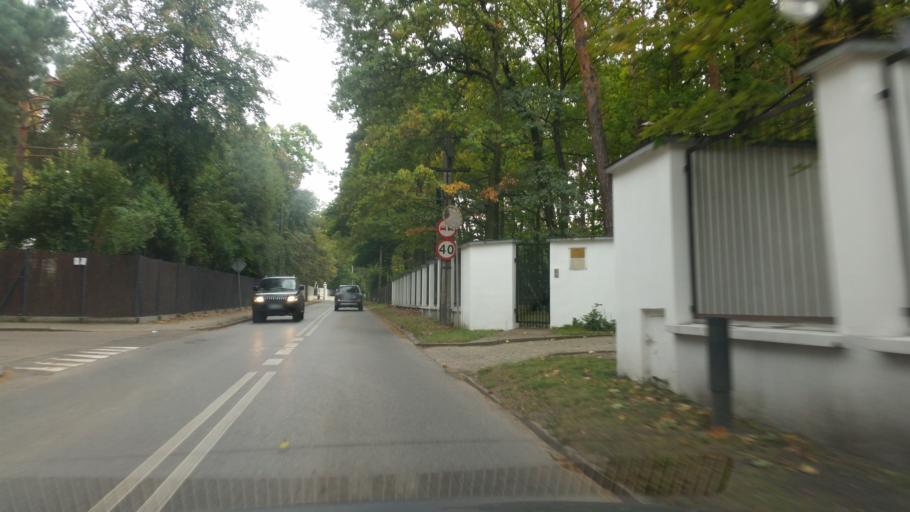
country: PL
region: Masovian Voivodeship
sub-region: Powiat piaseczynski
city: Konstancin-Jeziorna
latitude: 52.0798
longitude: 21.0974
